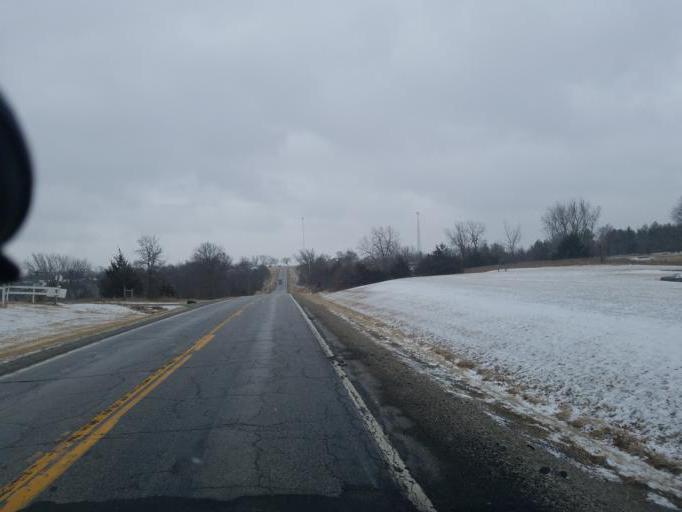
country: US
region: Missouri
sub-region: Putnam County
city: Unionville
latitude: 40.5218
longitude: -93.0121
